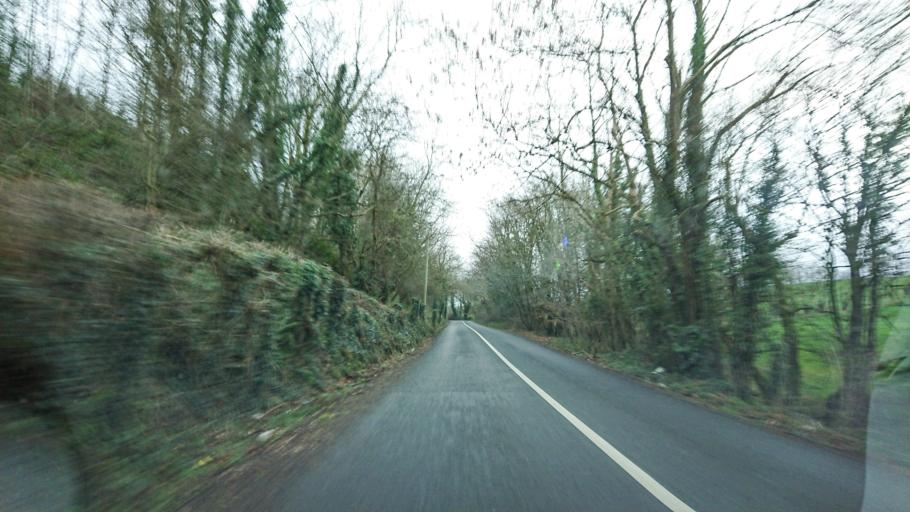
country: IE
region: Munster
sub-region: Waterford
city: Portlaw
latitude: 52.2651
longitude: -7.3996
